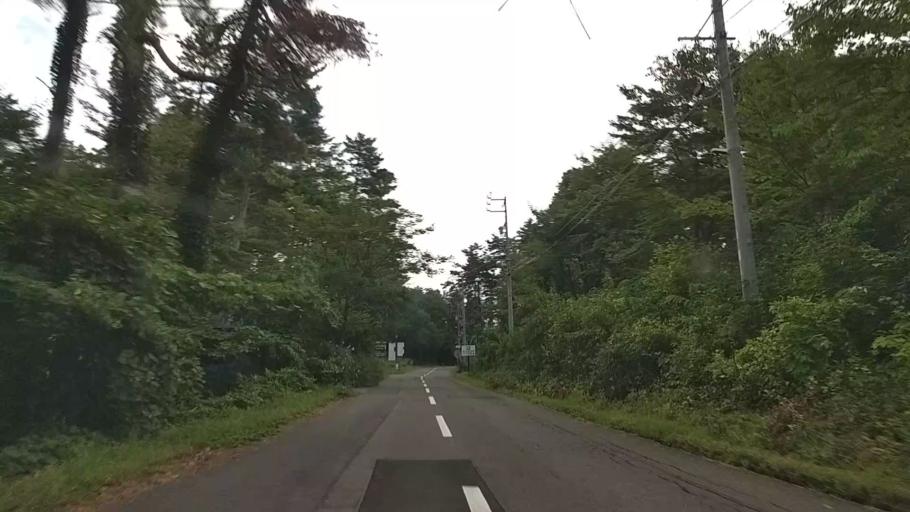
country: JP
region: Nagano
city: Iiyama
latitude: 36.8206
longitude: 138.3987
